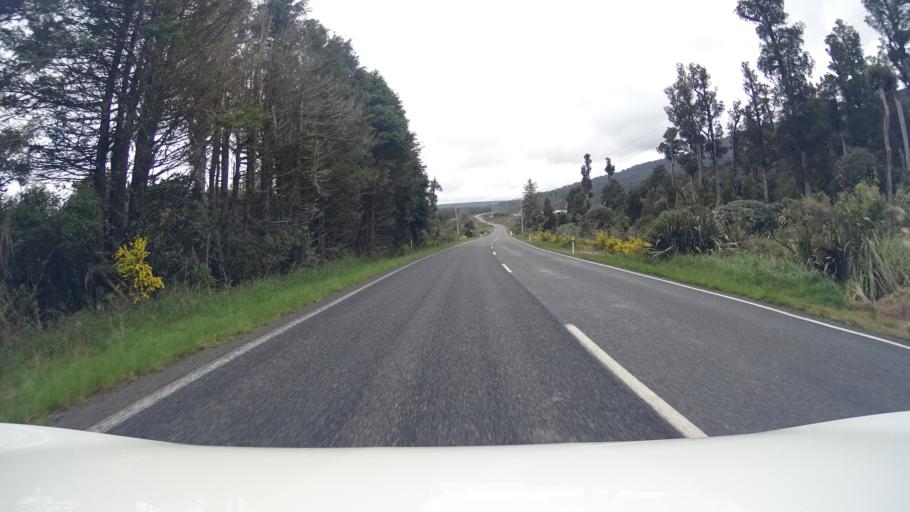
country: NZ
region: Manawatu-Wanganui
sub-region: Ruapehu District
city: Waiouru
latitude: -39.2361
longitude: 175.3917
